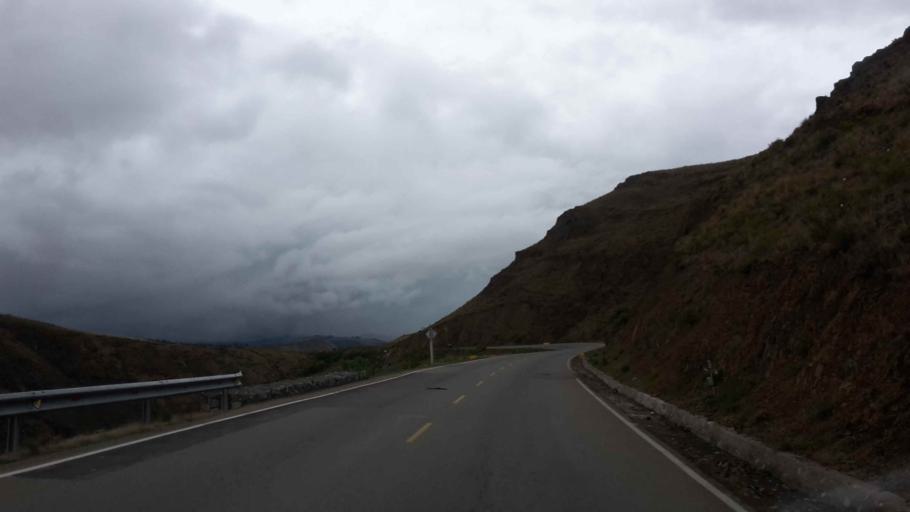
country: BO
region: Cochabamba
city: Punata
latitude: -17.4842
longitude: -65.7797
